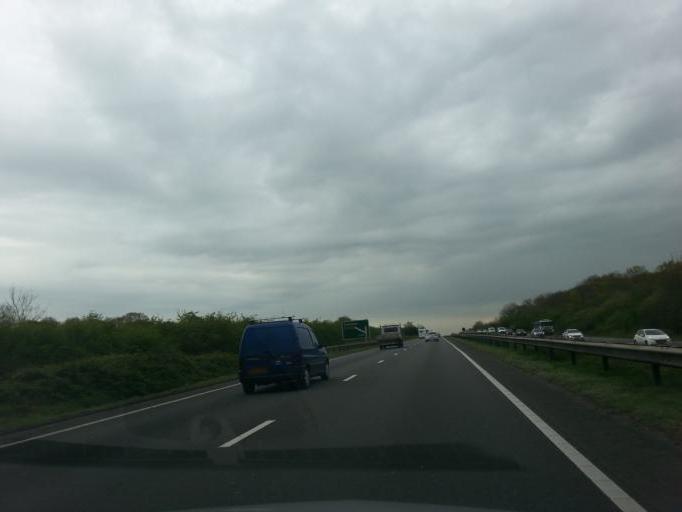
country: GB
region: England
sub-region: District of Rutland
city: Clipsham
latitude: 52.7193
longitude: -0.5950
